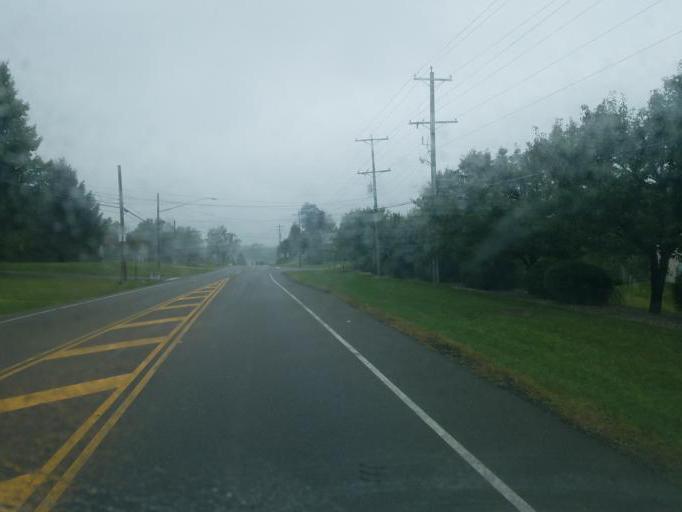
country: US
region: Ohio
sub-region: Licking County
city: Johnstown
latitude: 40.1597
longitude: -82.6905
